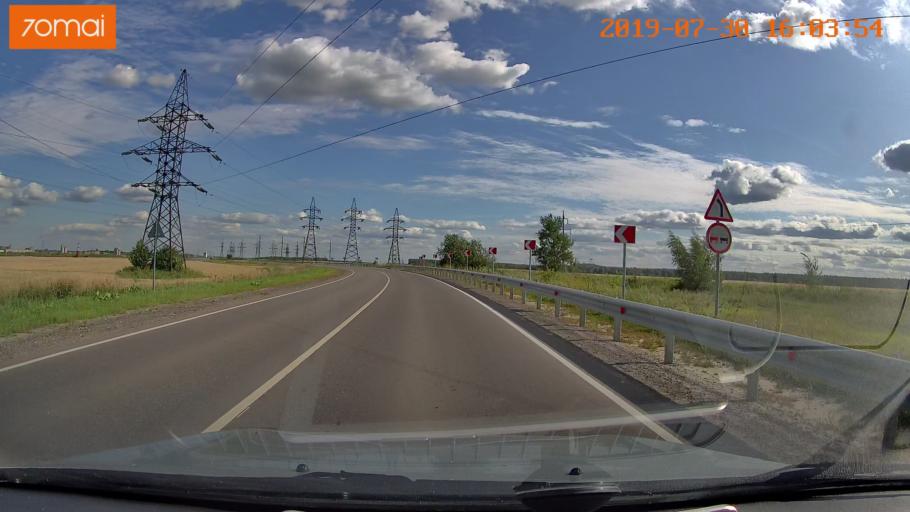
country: RU
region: Moskovskaya
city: Voskresensk
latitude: 55.2861
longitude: 38.7003
